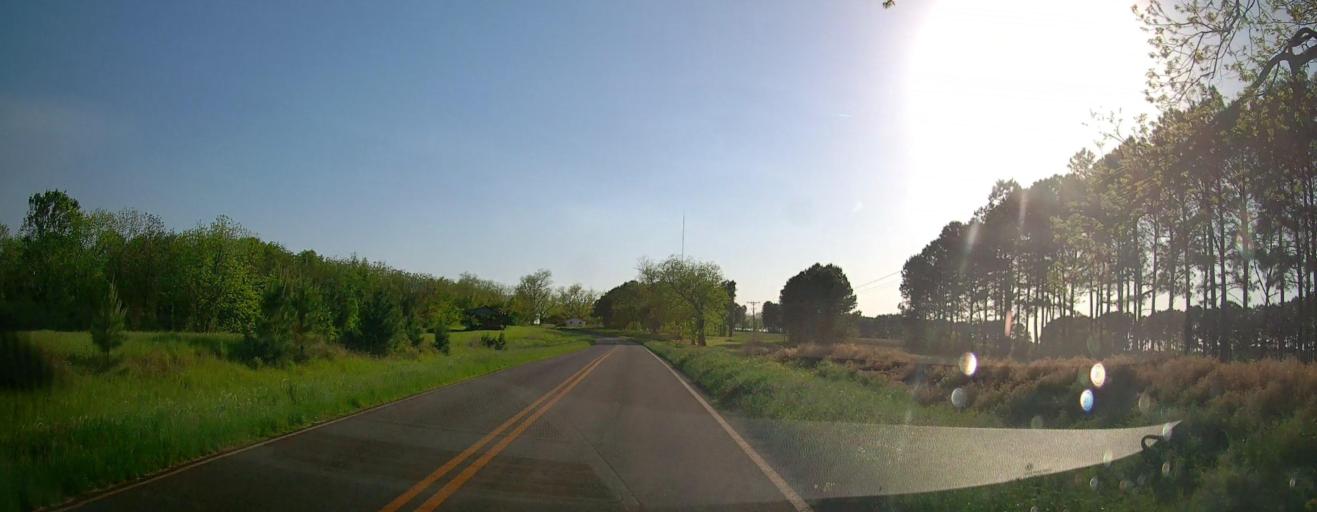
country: US
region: Georgia
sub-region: Macon County
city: Montezuma
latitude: 32.3351
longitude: -83.9545
